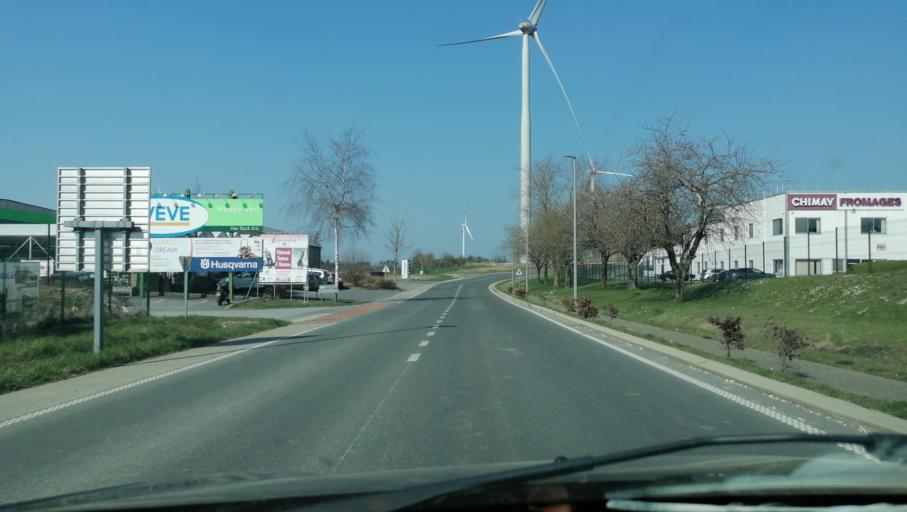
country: BE
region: Wallonia
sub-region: Province du Hainaut
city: Chimay
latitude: 50.0366
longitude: 4.3759
